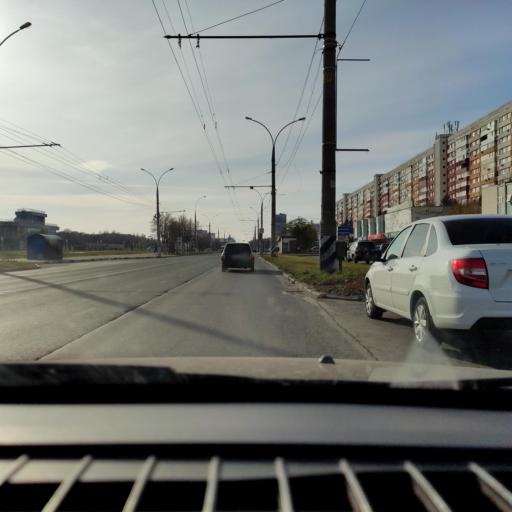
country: RU
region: Samara
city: Tol'yatti
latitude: 53.5145
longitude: 49.2725
